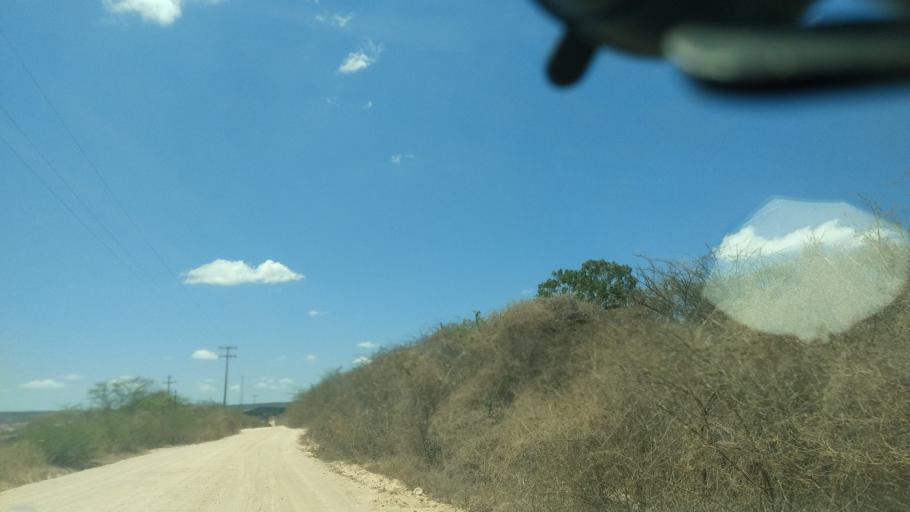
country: BR
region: Rio Grande do Norte
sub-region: Cerro Cora
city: Cerro Cora
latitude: -6.0271
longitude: -36.3372
